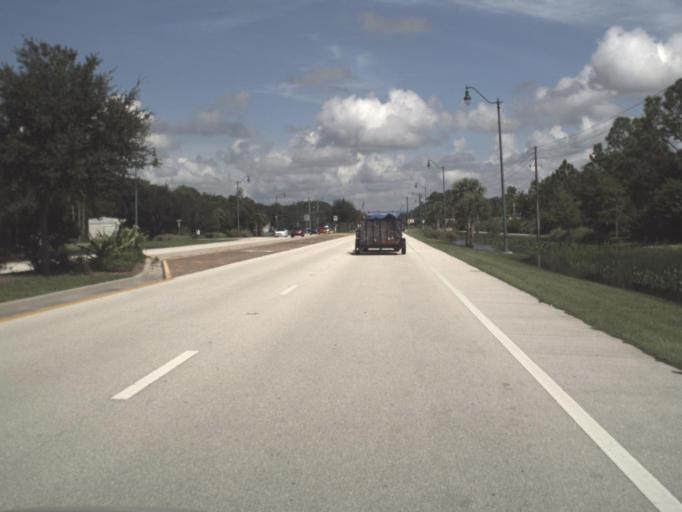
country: US
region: Florida
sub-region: Sarasota County
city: North Port
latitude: 27.0830
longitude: -82.1555
